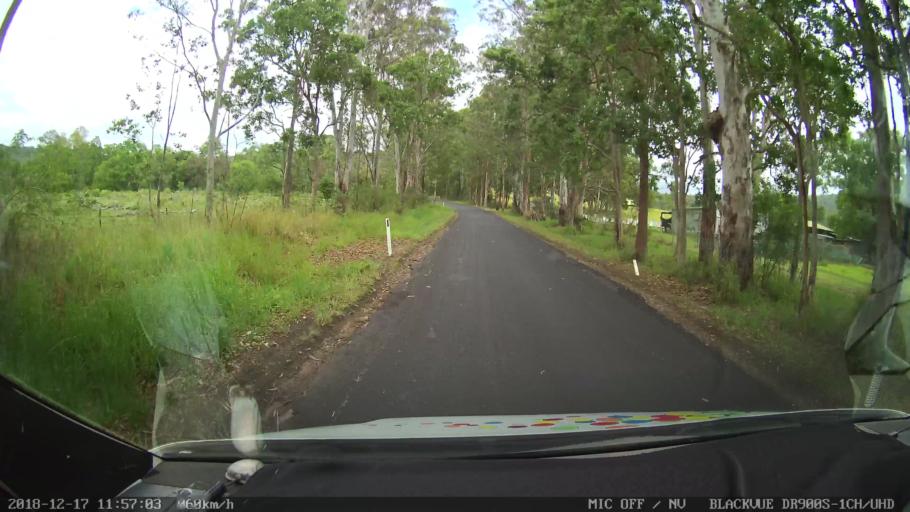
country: AU
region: New South Wales
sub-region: Kyogle
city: Kyogle
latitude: -28.5426
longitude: 152.5765
